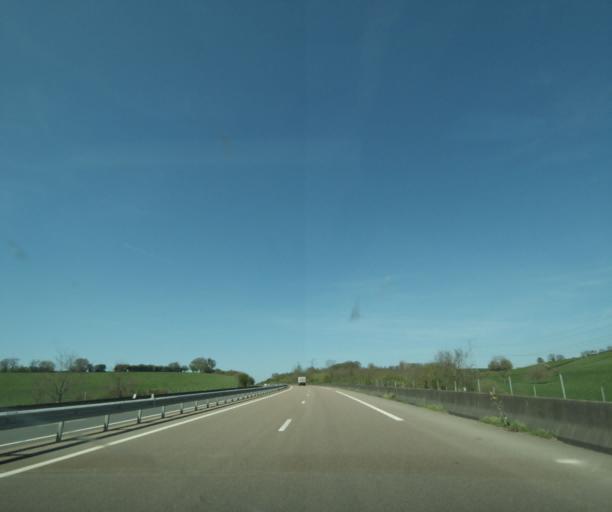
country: FR
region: Bourgogne
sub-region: Departement de la Nievre
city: Pougues-les-Eaux
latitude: 47.0805
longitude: 3.1223
